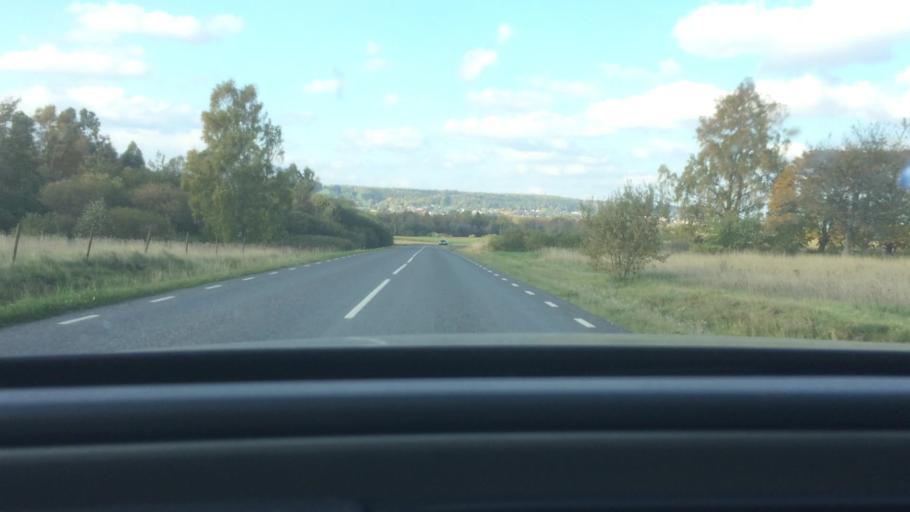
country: SE
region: Vaestra Goetaland
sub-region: Falkopings Kommun
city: Falkoeping
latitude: 58.1462
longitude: 13.5446
